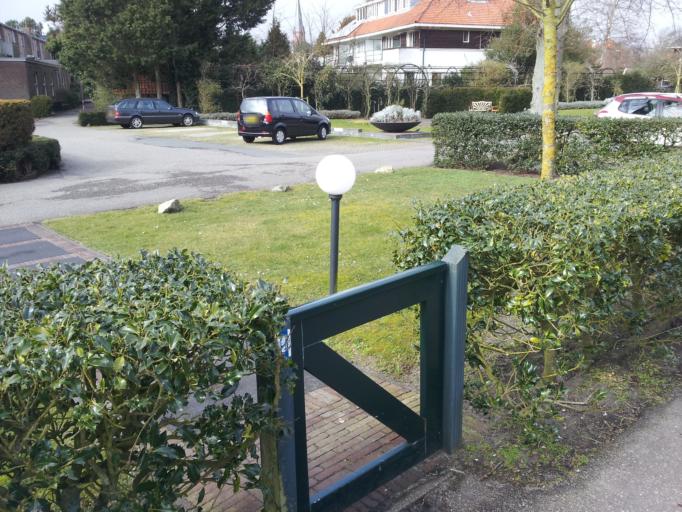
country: NL
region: South Holland
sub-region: Gemeente Wassenaar
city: Wassenaar
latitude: 52.1365
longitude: 4.3931
